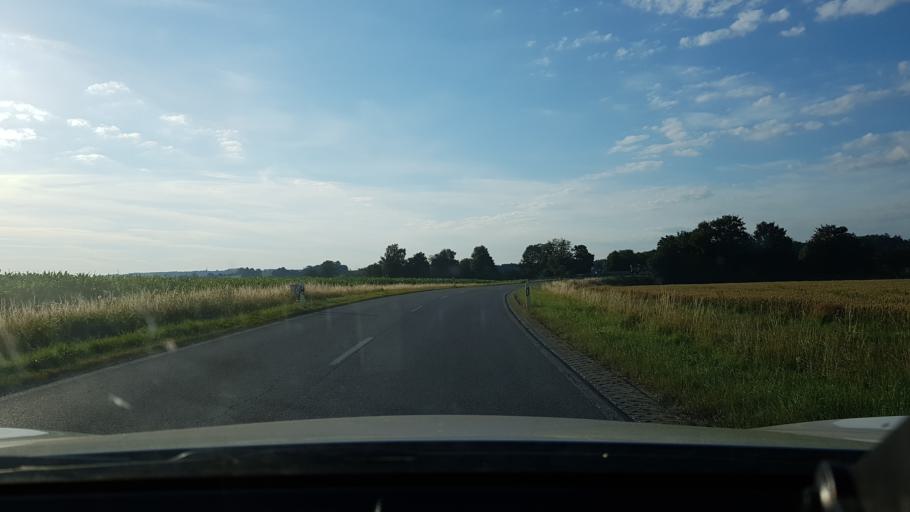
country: DE
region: Baden-Wuerttemberg
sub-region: Tuebingen Region
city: Maselheim
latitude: 48.1562
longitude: 9.8412
